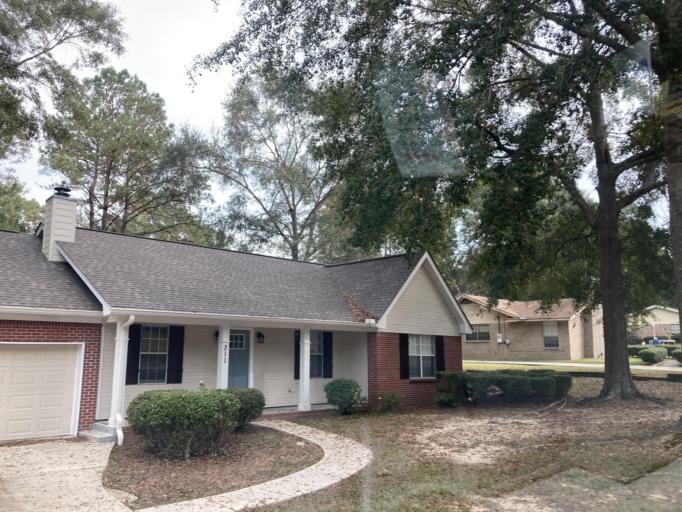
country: US
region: Mississippi
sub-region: Lamar County
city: West Hattiesburg
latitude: 31.2816
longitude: -89.3629
